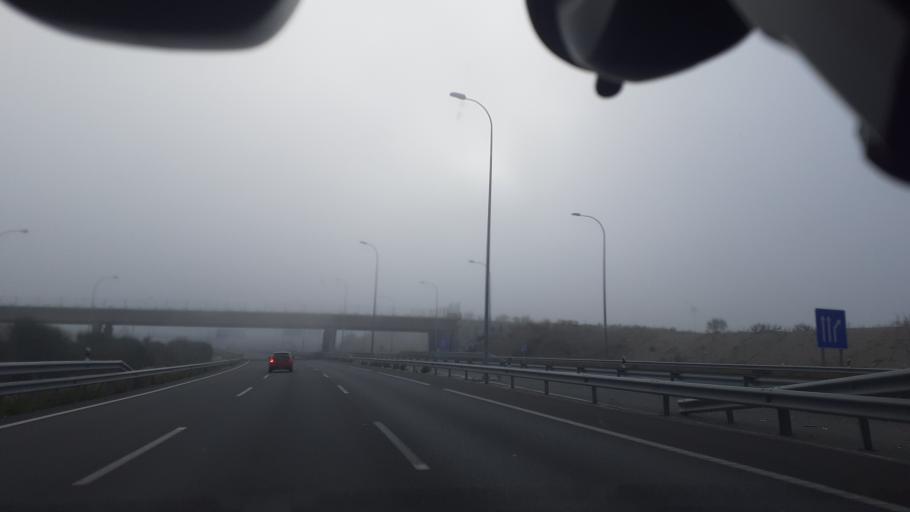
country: ES
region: Madrid
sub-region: Provincia de Madrid
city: Vicalvaro
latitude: 40.3885
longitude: -3.5845
